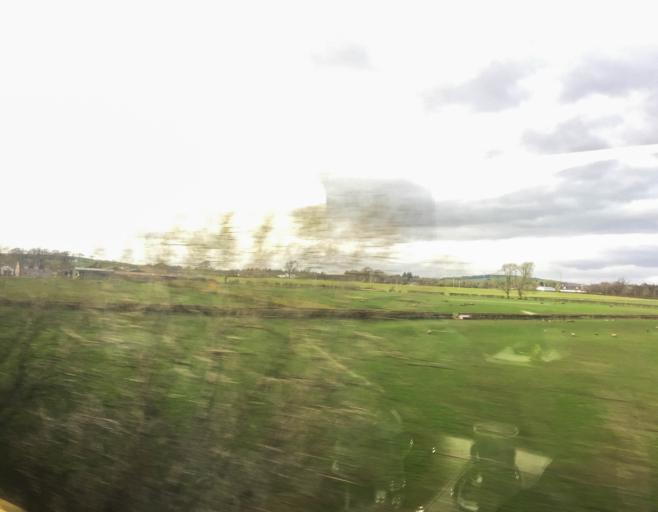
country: GB
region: Scotland
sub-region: Dumfries and Galloway
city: Annan
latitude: 55.0641
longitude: -3.2283
